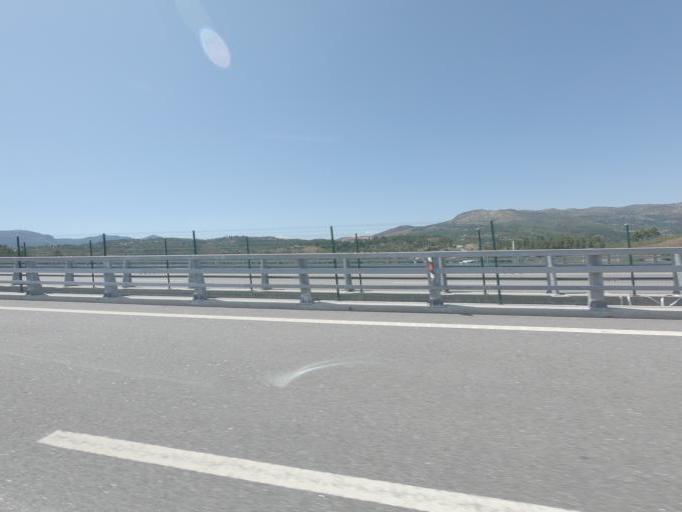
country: PT
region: Vila Real
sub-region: Vila Real
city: Vila Real
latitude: 41.2690
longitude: -7.7848
